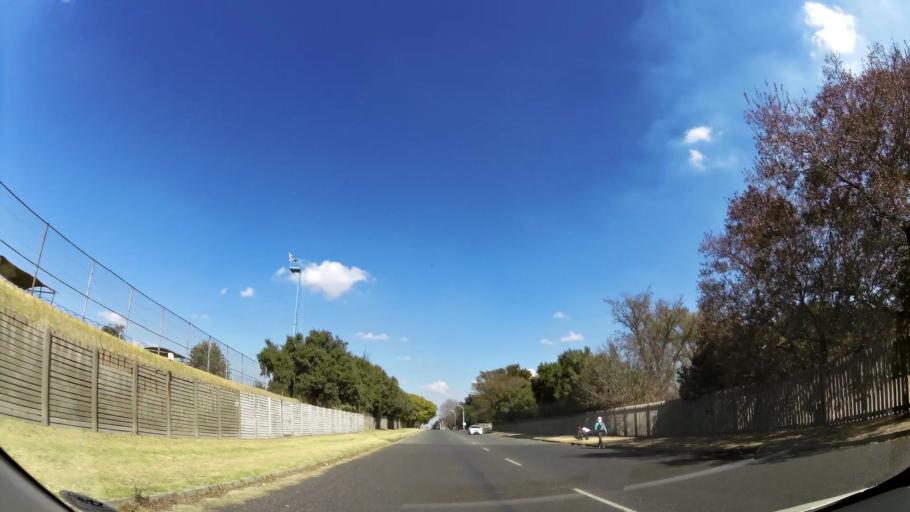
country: ZA
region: Mpumalanga
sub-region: Nkangala District Municipality
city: Witbank
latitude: -25.8691
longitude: 29.2179
